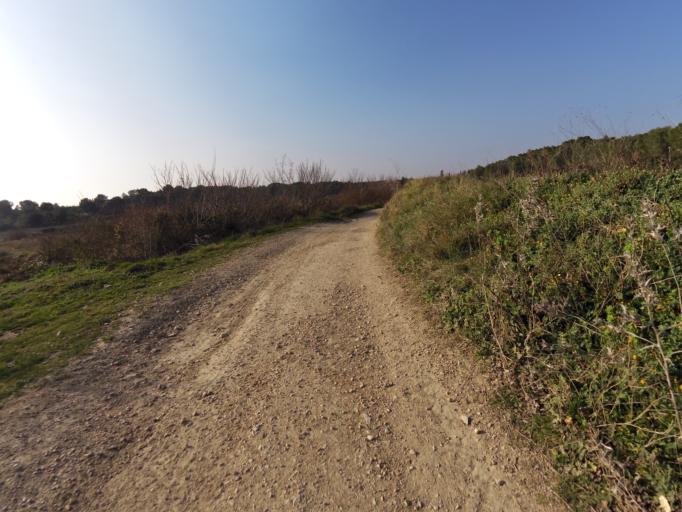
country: FR
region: Languedoc-Roussillon
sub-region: Departement du Gard
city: Gallargues-le-Montueux
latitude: 43.7325
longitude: 4.1609
